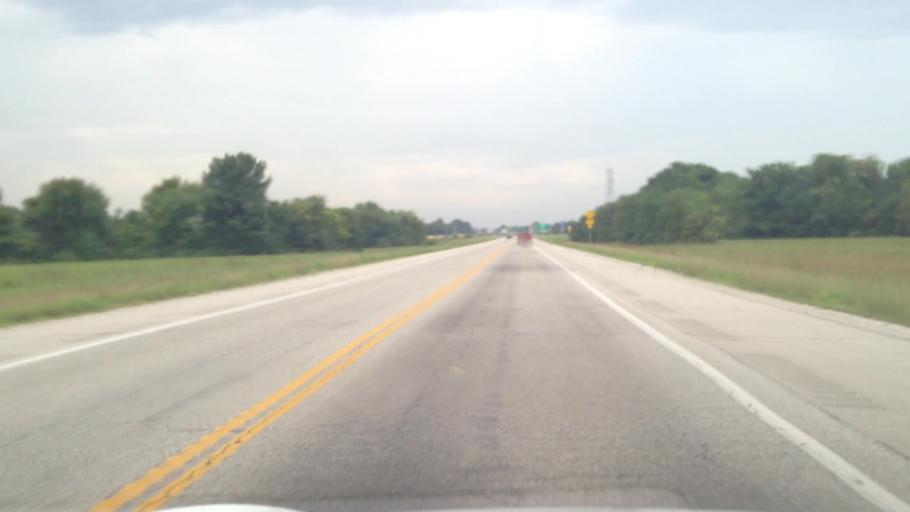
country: US
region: Kansas
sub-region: Cherokee County
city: Baxter Springs
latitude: 37.0800
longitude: -94.7110
